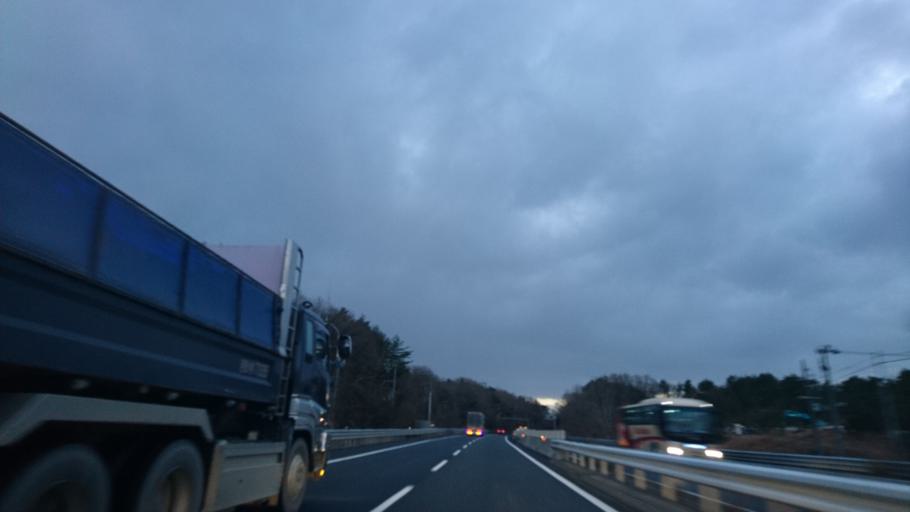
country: JP
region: Mie
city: Nabari
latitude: 34.6337
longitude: 135.9993
